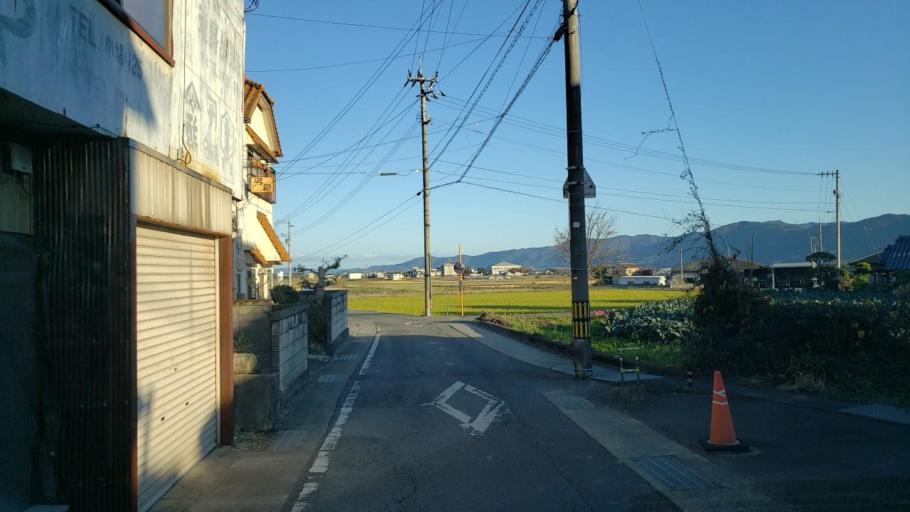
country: JP
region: Tokushima
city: Kamojimacho-jogejima
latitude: 34.0909
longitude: 134.2550
